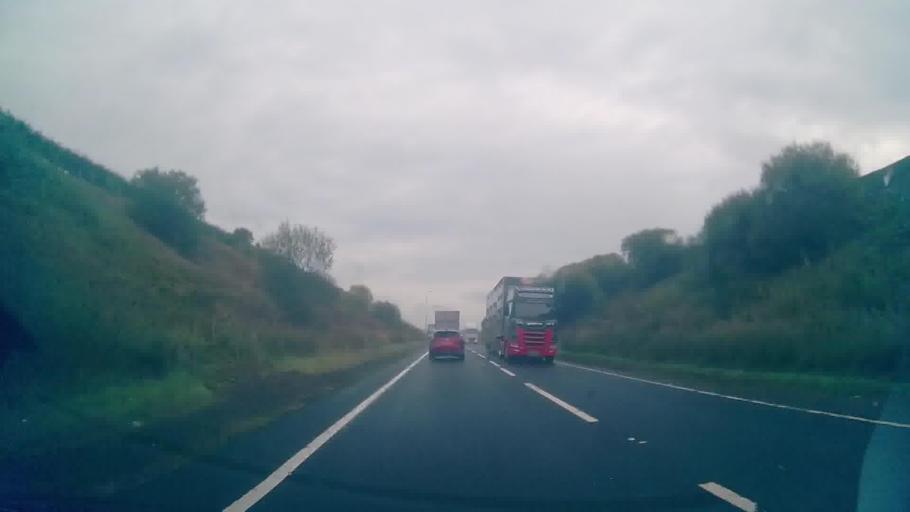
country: GB
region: Scotland
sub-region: Dumfries and Galloway
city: Lochmaben
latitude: 55.0339
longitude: -3.4143
